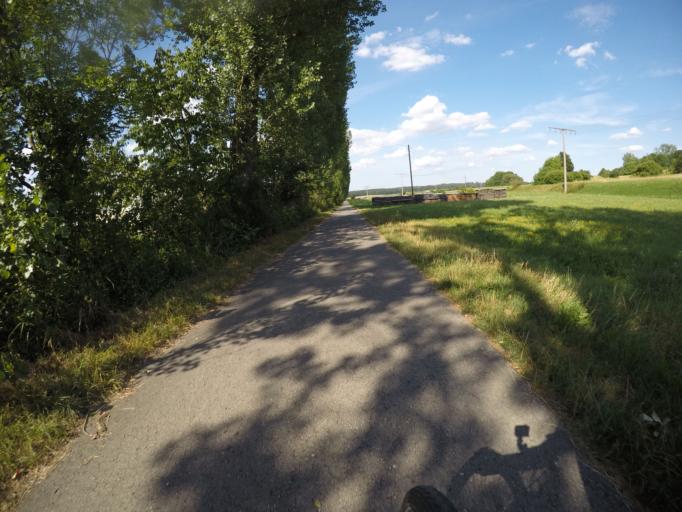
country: DE
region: Baden-Wuerttemberg
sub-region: Regierungsbezirk Stuttgart
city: Gartringen
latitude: 48.6289
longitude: 8.9253
